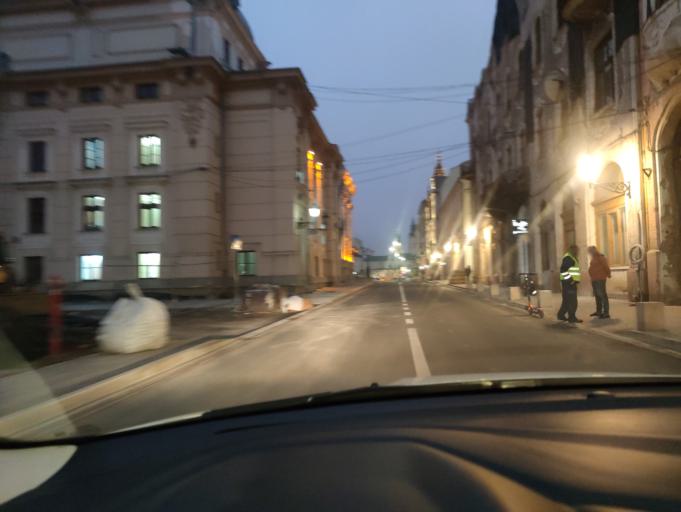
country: RO
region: Bihor
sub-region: Comuna Biharea
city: Oradea
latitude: 47.0578
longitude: 21.9312
